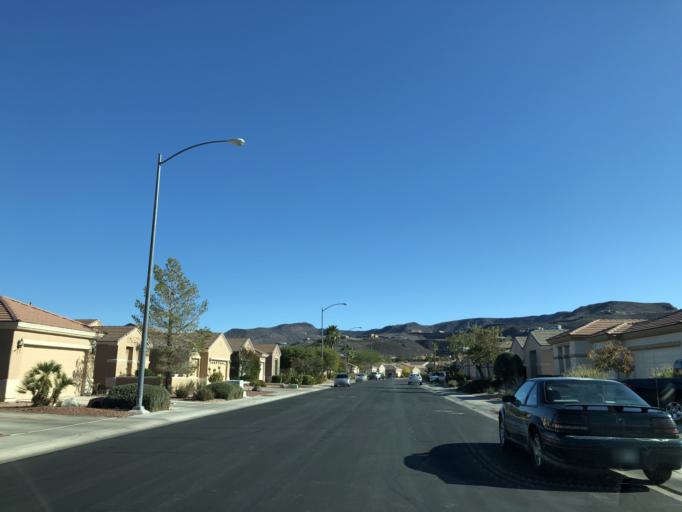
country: US
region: Nevada
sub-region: Clark County
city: Whitney
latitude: 36.0040
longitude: -115.0712
